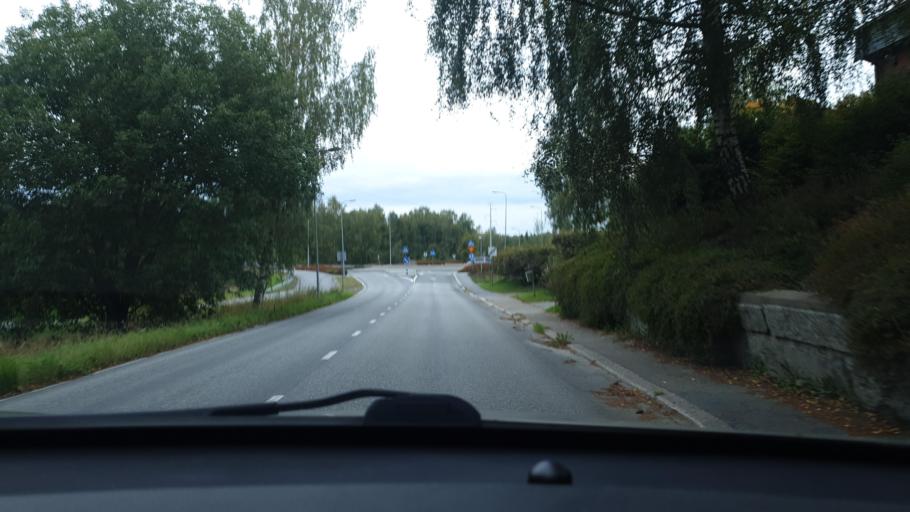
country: FI
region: Ostrobothnia
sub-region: Vaasa
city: Korsholm
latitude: 63.0980
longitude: 21.6614
